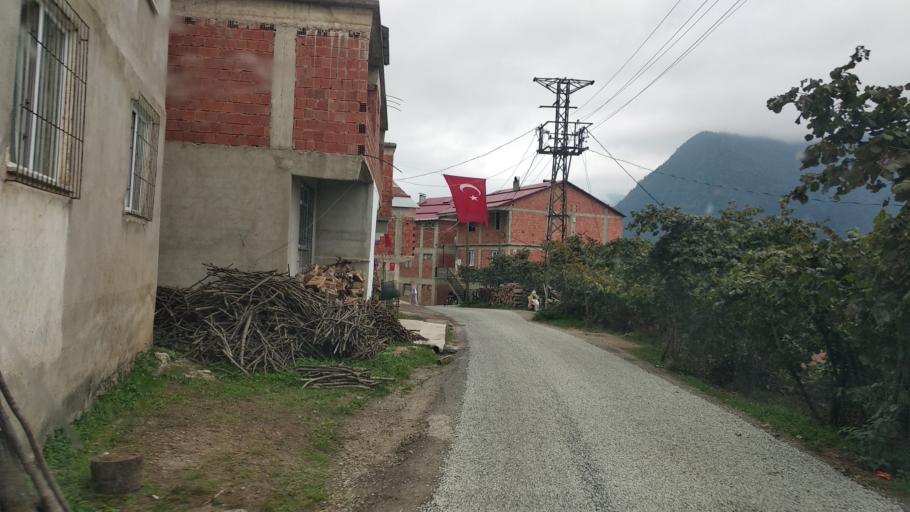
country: TR
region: Giresun
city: Dogankent
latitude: 40.7468
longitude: 38.9875
